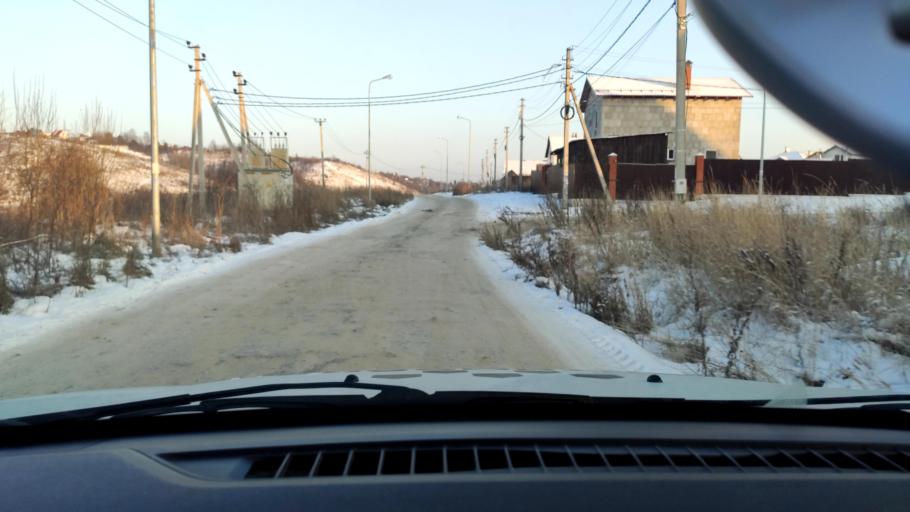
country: RU
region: Perm
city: Perm
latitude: 58.0282
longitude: 56.3460
